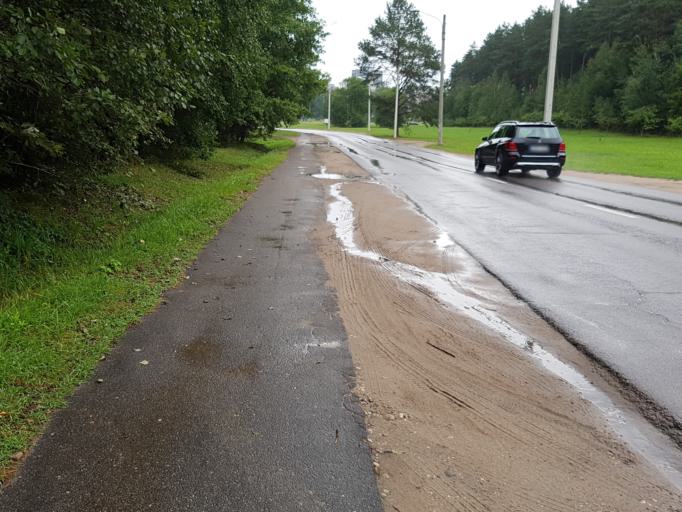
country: LT
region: Vilnius County
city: Lazdynai
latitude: 54.6680
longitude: 25.1969
